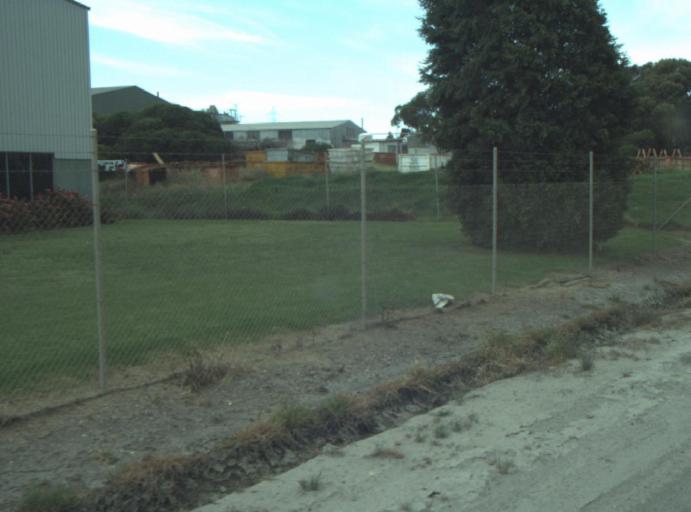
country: AU
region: Victoria
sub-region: Greater Geelong
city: Leopold
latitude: -38.1603
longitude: 144.4300
